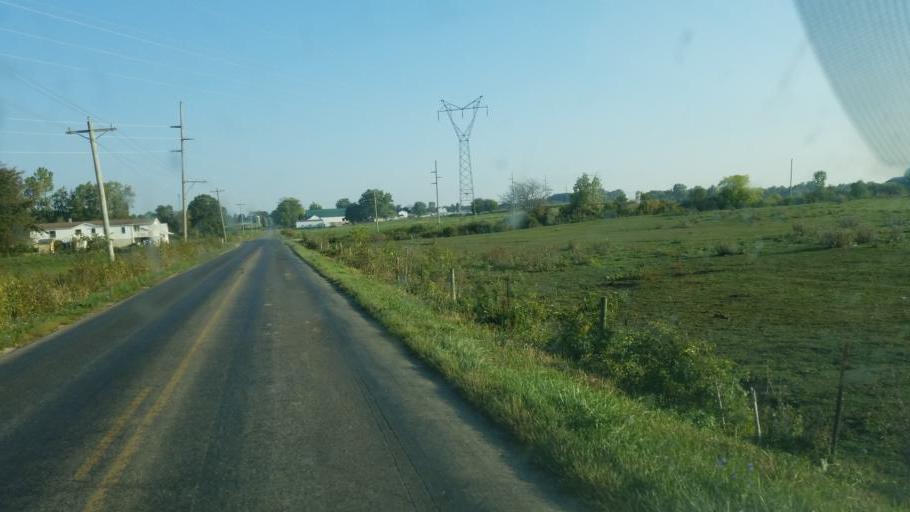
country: US
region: Indiana
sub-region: LaGrange County
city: Lagrange
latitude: 41.6113
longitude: -85.4243
